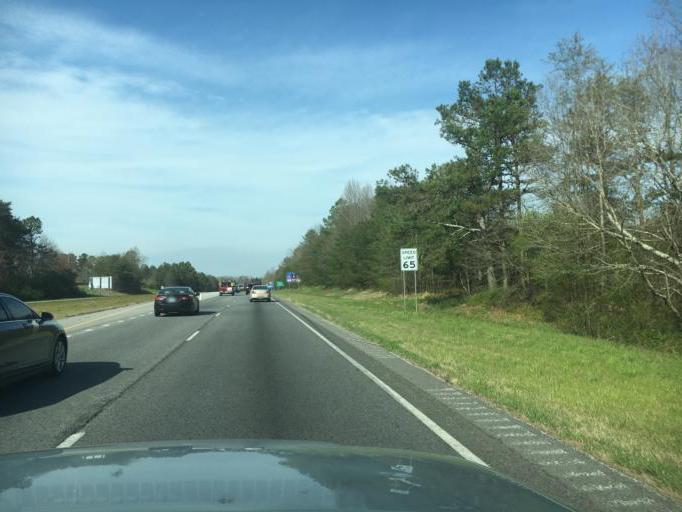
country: US
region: Georgia
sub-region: Banks County
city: Alto
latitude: 34.5009
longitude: -83.5719
